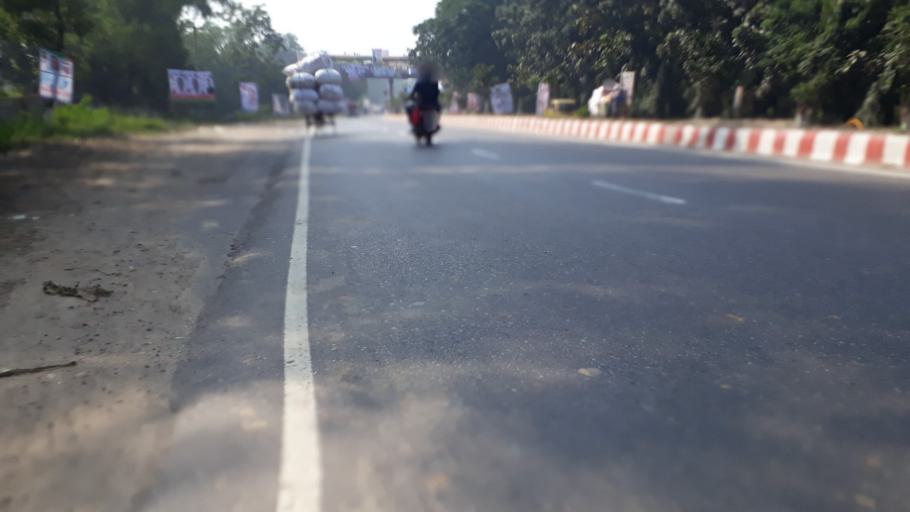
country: BD
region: Dhaka
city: Tungi
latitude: 23.8670
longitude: 90.2714
